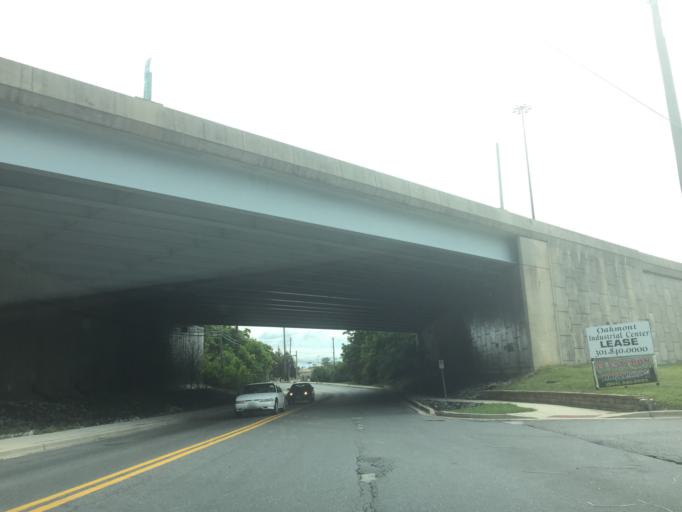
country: US
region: Maryland
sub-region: Montgomery County
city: Derwood
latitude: 39.1282
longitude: -77.1742
